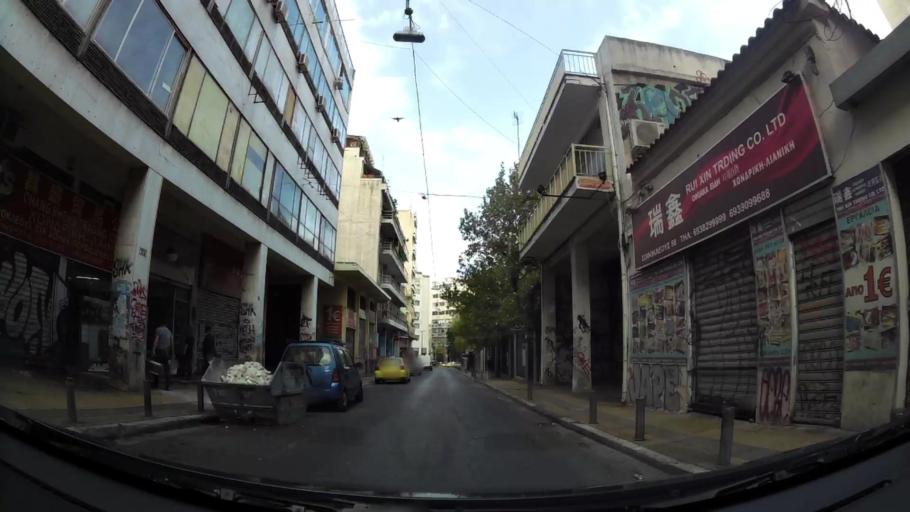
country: GR
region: Attica
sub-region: Nomarchia Athinas
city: Athens
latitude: 37.9816
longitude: 23.7242
